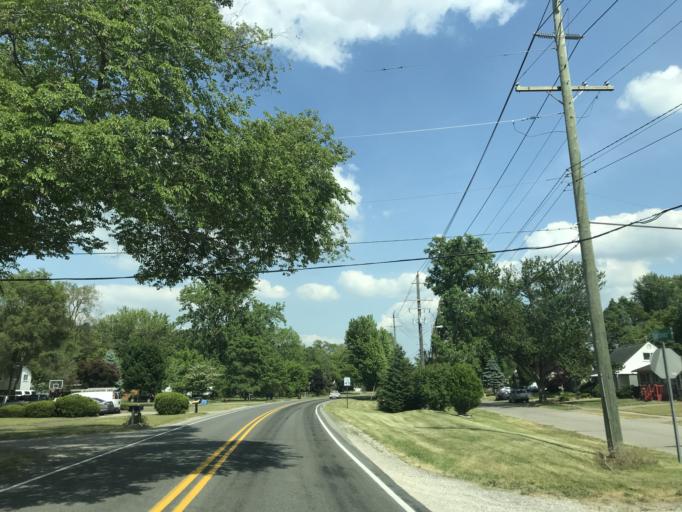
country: US
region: Michigan
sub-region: Washtenaw County
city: Ypsilanti
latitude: 42.2612
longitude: -83.5906
